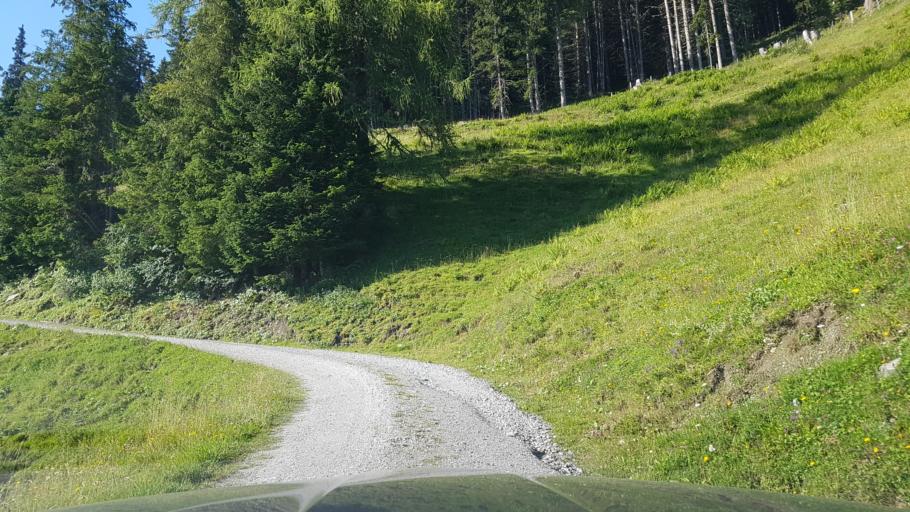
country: AT
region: Salzburg
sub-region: Politischer Bezirk Sankt Johann im Pongau
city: Dorfgastein
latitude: 47.2448
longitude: 13.0735
